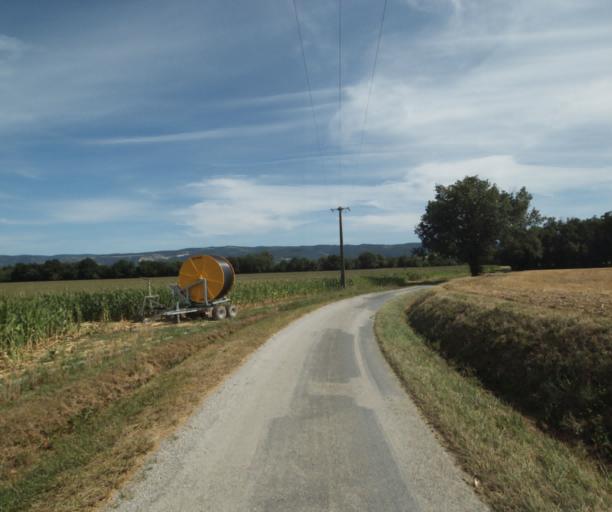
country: FR
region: Midi-Pyrenees
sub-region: Departement du Tarn
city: Soreze
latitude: 43.5054
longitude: 2.0629
